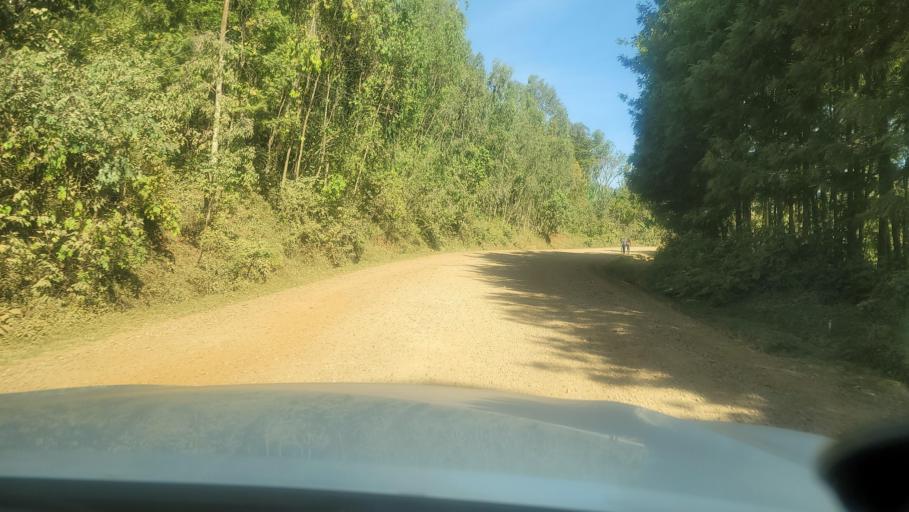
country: ET
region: Oromiya
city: Agaro
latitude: 7.8027
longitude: 36.4652
